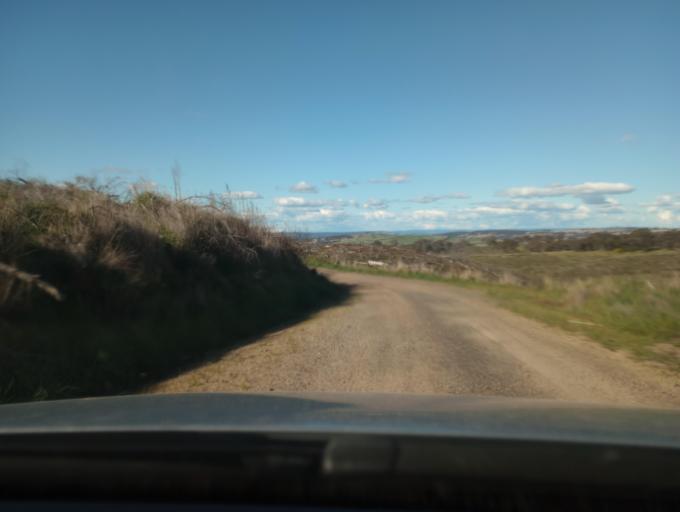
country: AU
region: New South Wales
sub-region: Blayney
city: Blayney
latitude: -33.4215
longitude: 149.3143
